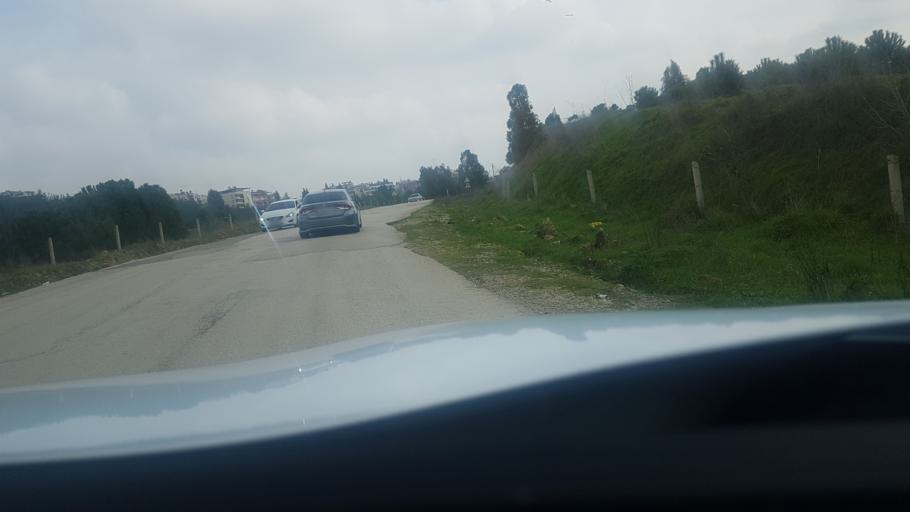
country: TR
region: Adana
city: Seyhan
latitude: 37.0617
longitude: 35.2568
